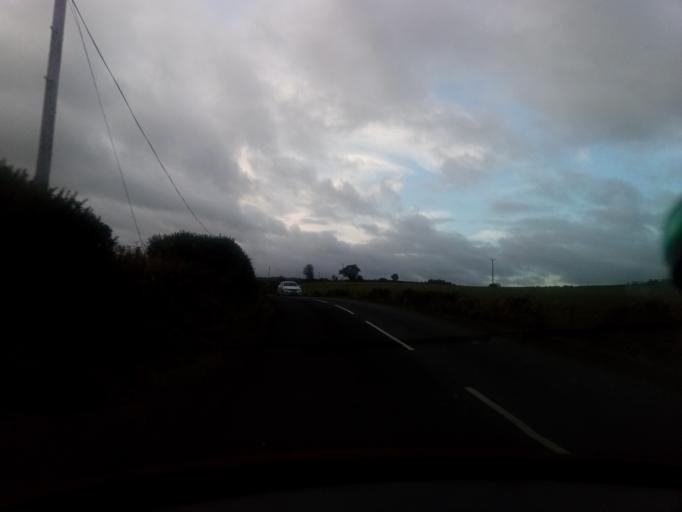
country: GB
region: Scotland
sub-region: The Scottish Borders
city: Jedburgh
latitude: 55.4481
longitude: -2.5727
